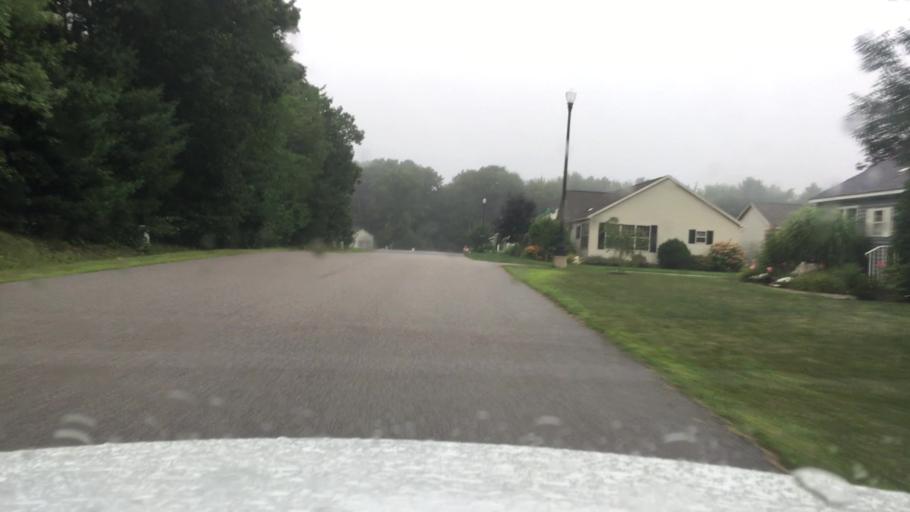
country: US
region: Maine
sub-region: Cumberland County
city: Scarborough
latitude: 43.5976
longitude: -70.3138
